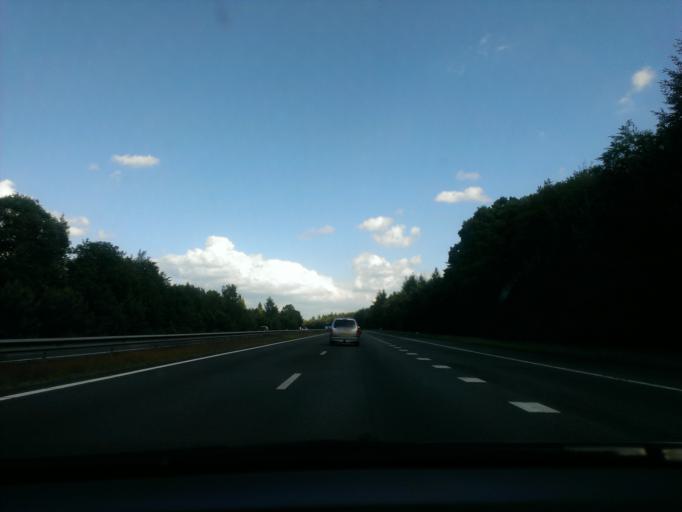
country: NL
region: Gelderland
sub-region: Gemeente Apeldoorn
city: Beekbergen
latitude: 52.1764
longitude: 5.9457
